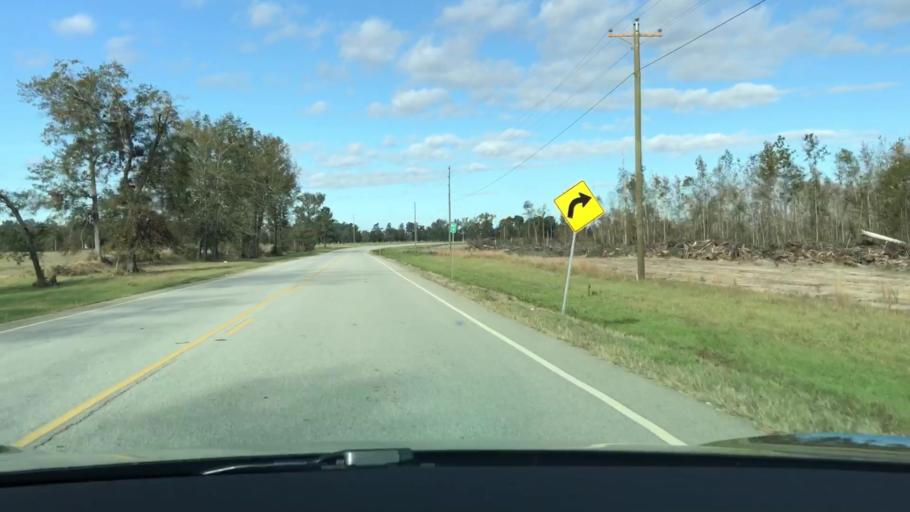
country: US
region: Georgia
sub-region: Jefferson County
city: Wrens
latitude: 33.1172
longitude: -82.4395
